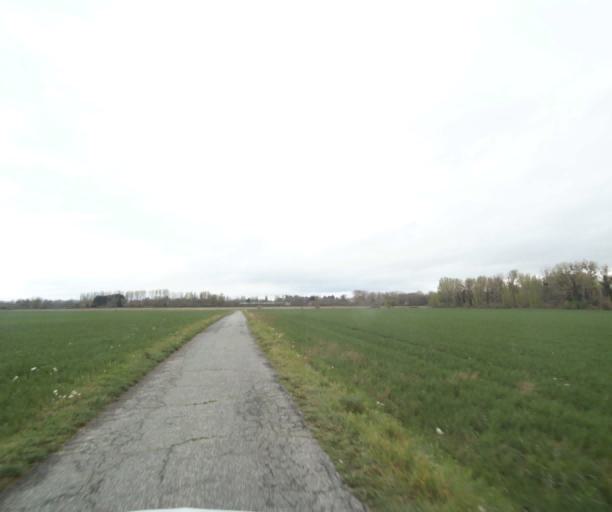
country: FR
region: Midi-Pyrenees
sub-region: Departement de l'Ariege
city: Saverdun
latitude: 43.2213
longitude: 1.5990
